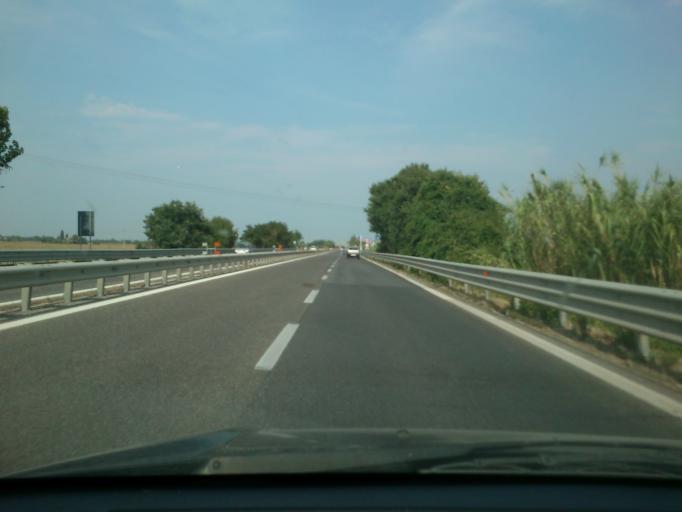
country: IT
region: The Marches
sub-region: Provincia di Pesaro e Urbino
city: Cuccurano
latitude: 43.7740
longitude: 12.9712
